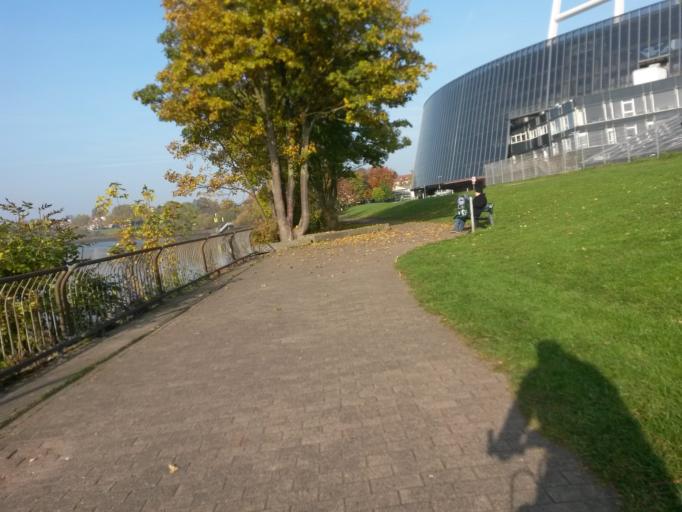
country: DE
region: Bremen
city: Bremen
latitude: 53.0651
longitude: 8.8366
